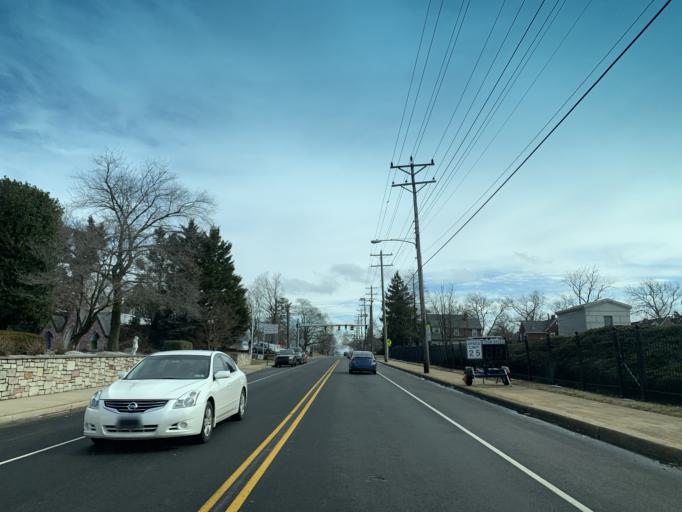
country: US
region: Delaware
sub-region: New Castle County
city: Elsmere
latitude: 39.7487
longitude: -75.5792
